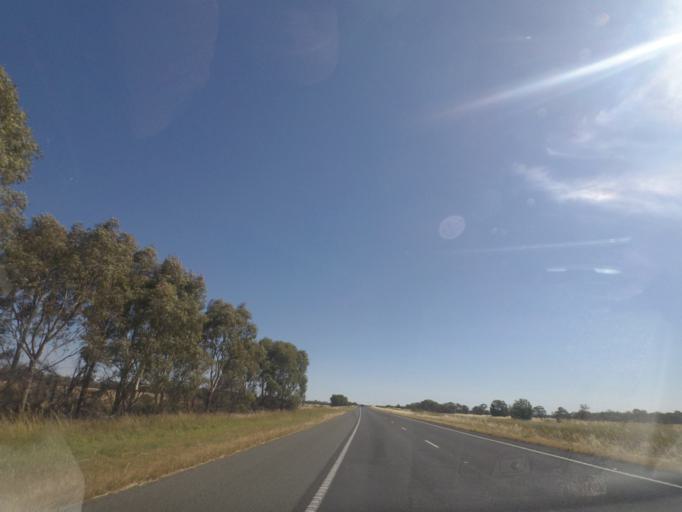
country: AU
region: Victoria
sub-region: Greater Shepparton
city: Shepparton
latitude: -36.6239
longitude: 145.3013
